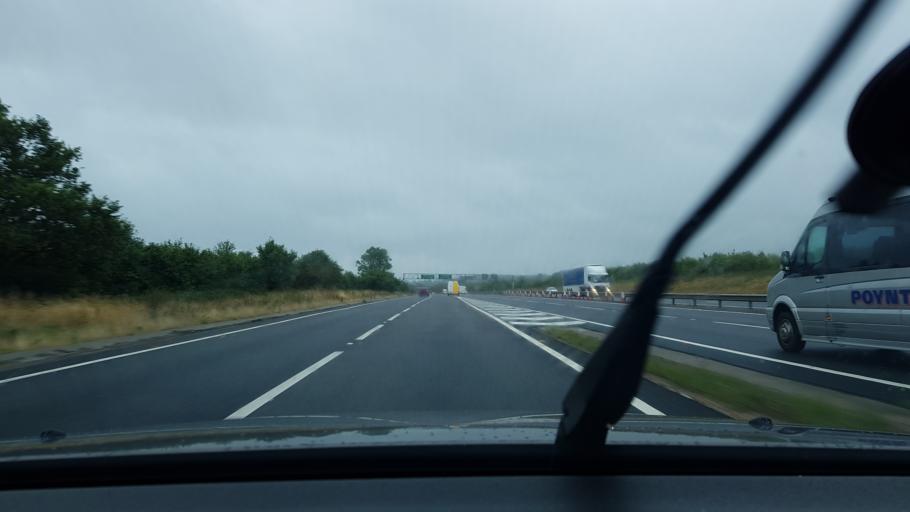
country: GB
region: England
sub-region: West Berkshire
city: Winterbourne
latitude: 51.4451
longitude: -1.3162
